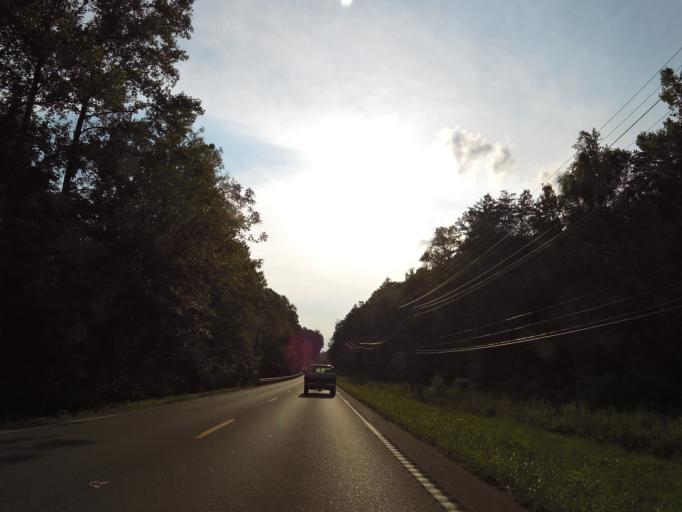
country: US
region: Tennessee
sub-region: Morgan County
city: Coalfield
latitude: 36.0392
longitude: -84.3881
